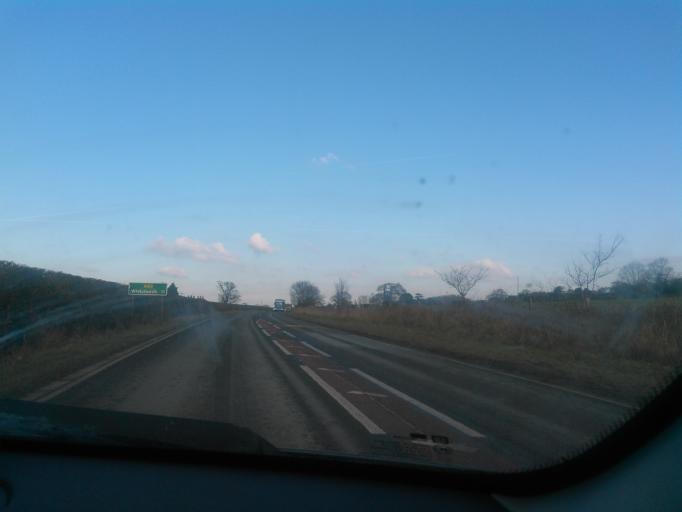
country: GB
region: England
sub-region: Shropshire
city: Clive
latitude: 52.8258
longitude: -2.6835
